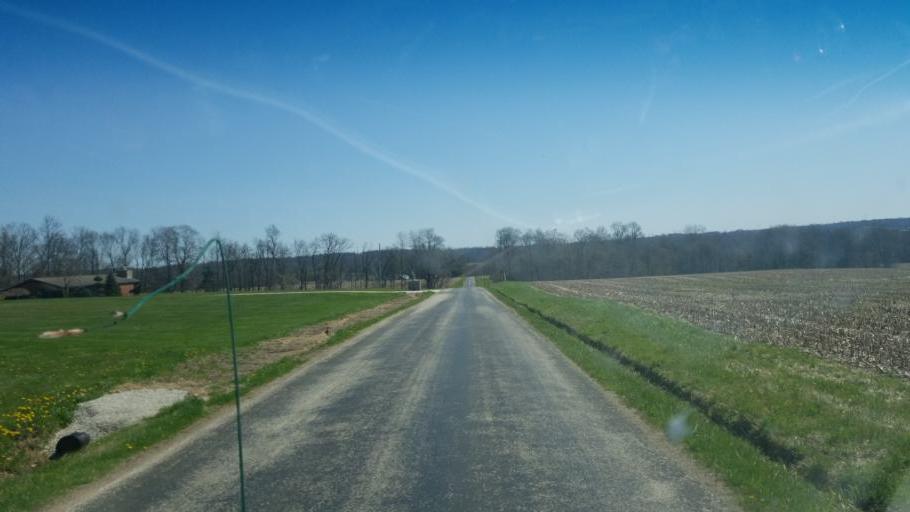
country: US
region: Ohio
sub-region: Richland County
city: Lincoln Heights
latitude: 40.8266
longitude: -82.4322
